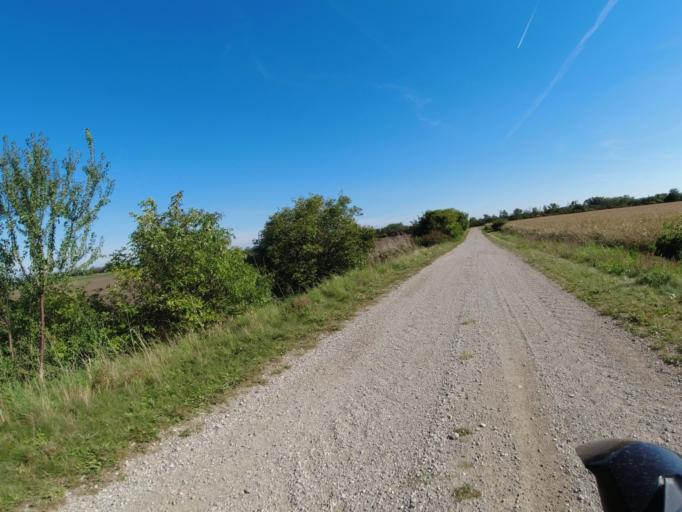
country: AT
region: Lower Austria
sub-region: Politischer Bezirk Baden
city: Trumau
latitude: 48.0181
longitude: 16.3295
